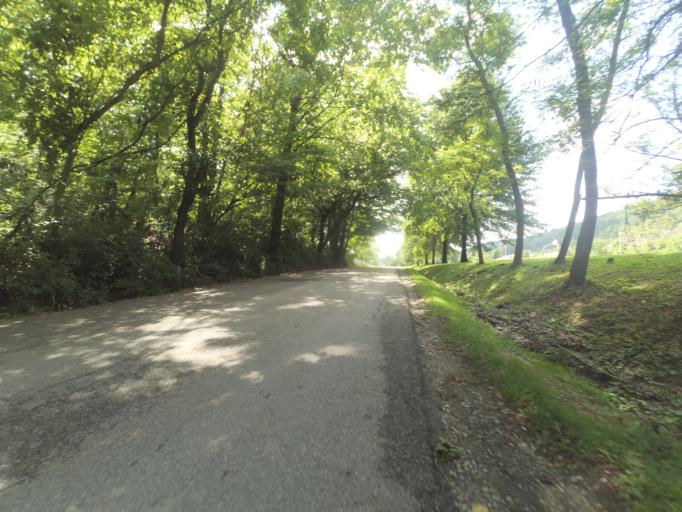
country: US
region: West Virginia
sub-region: Cabell County
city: Pea Ridge
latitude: 38.4180
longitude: -82.3546
